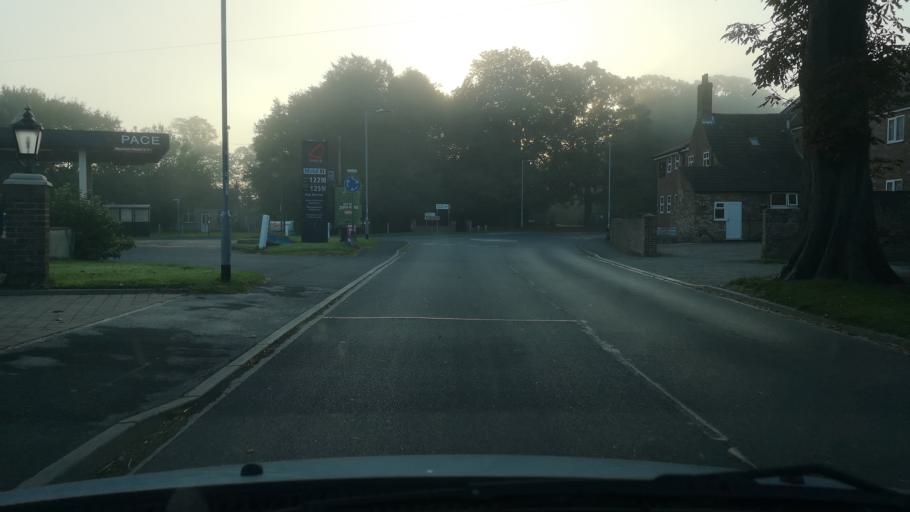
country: GB
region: England
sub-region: East Riding of Yorkshire
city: Skelton
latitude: 53.6908
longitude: -0.8337
